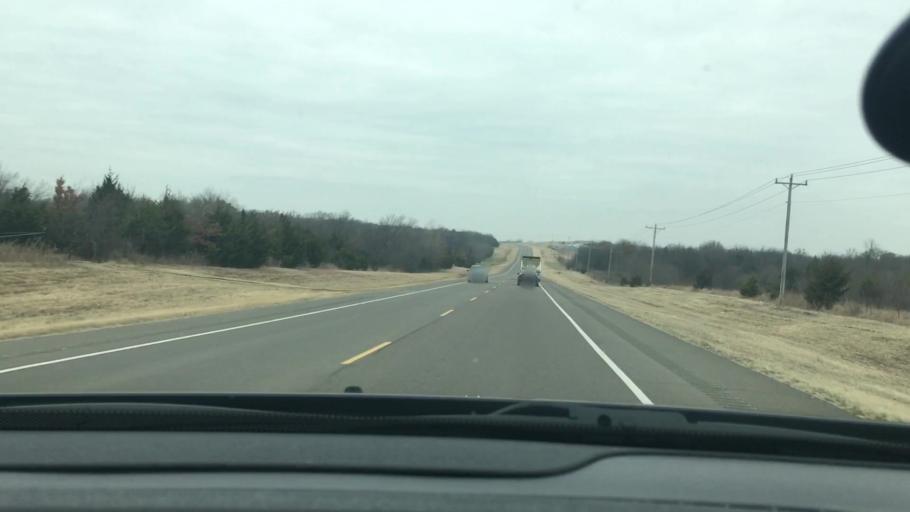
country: US
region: Oklahoma
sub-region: Murray County
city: Davis
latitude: 34.5141
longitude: -97.2019
